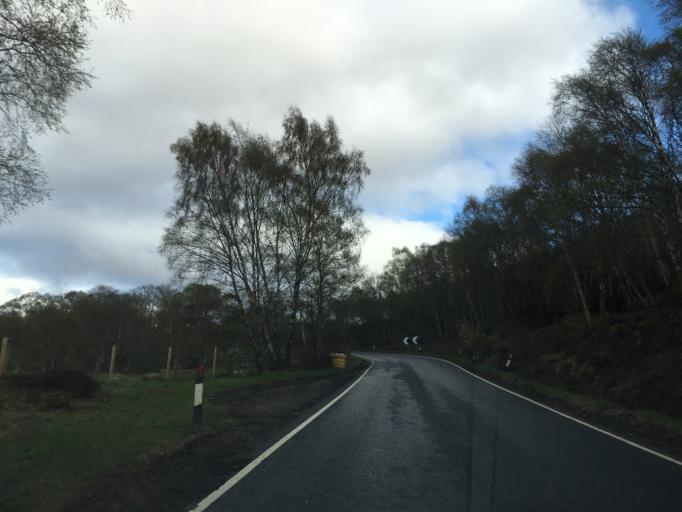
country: GB
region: Scotland
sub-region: Highland
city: Kingussie
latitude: 57.0076
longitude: -4.2612
